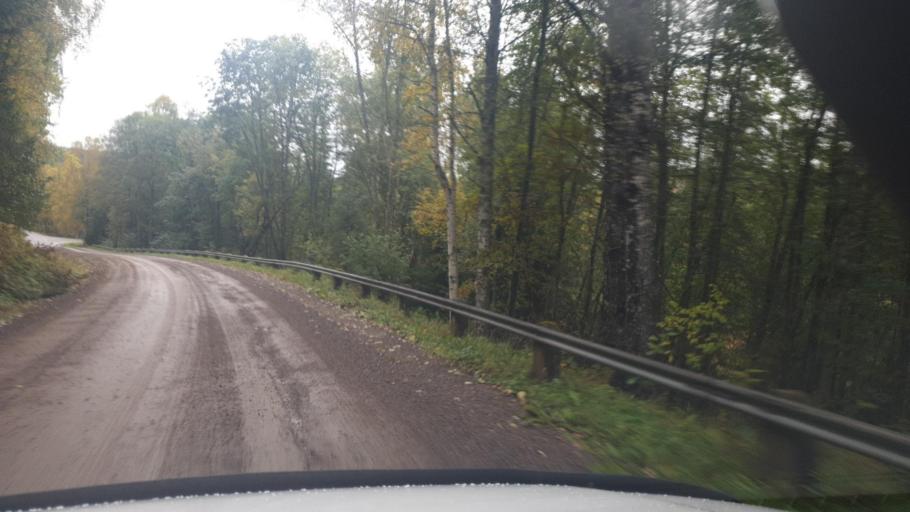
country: SE
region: Vaermland
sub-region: Arvika Kommun
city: Arvika
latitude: 60.0136
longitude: 12.6452
